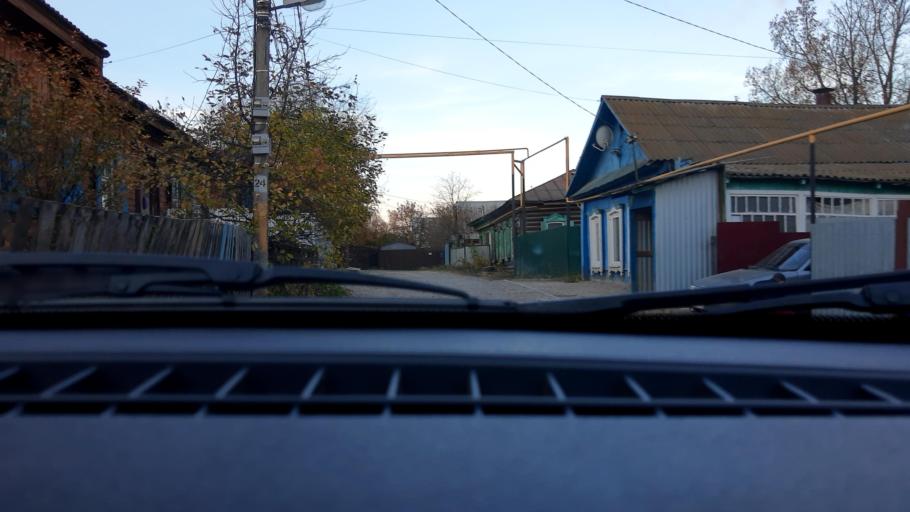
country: RU
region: Bashkortostan
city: Ufa
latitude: 54.7393
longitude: 55.9265
